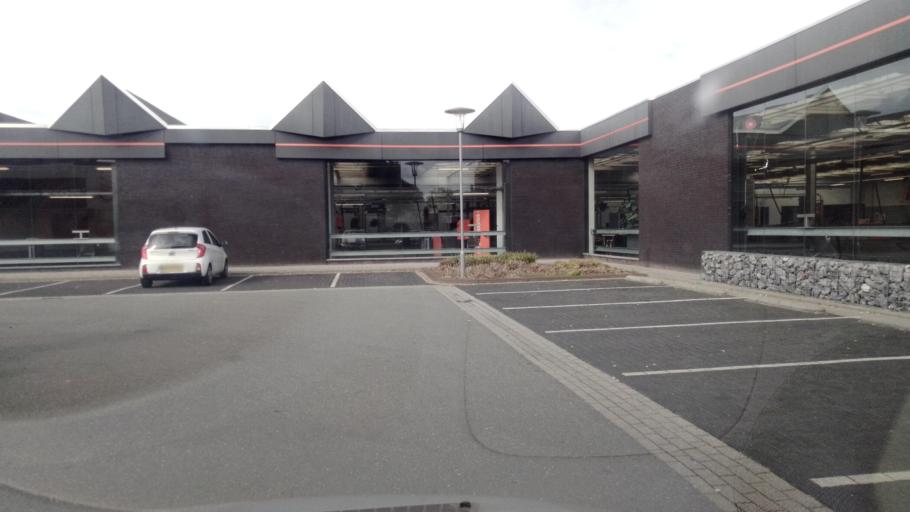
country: NL
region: North Brabant
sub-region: Gemeente Helmond
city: Helmond
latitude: 51.4757
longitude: 5.6342
